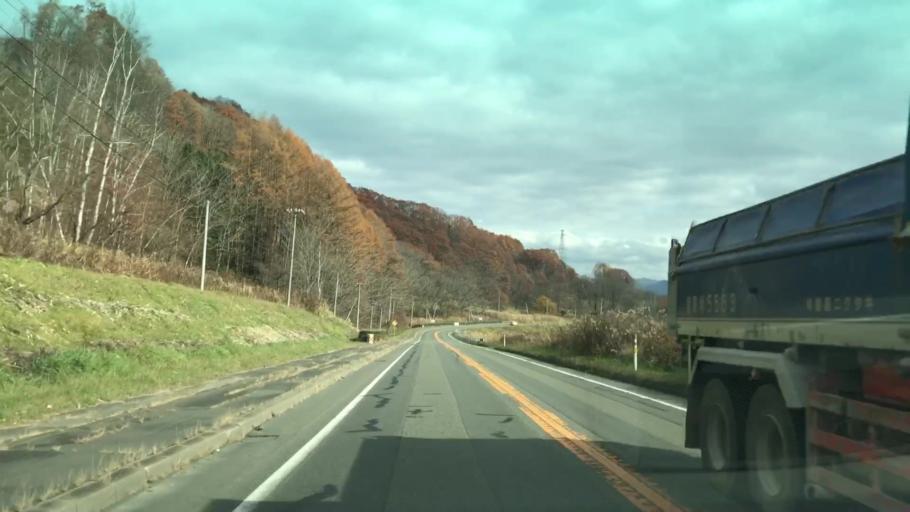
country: JP
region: Hokkaido
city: Shizunai-furukawacho
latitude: 42.7203
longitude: 142.2692
